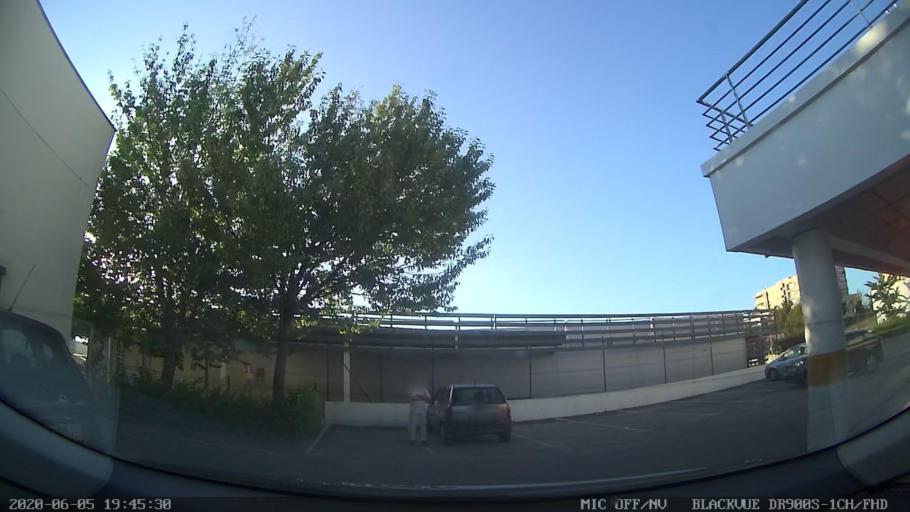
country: PT
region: Porto
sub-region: Valongo
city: Ermesinde
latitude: 41.2132
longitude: -8.5505
